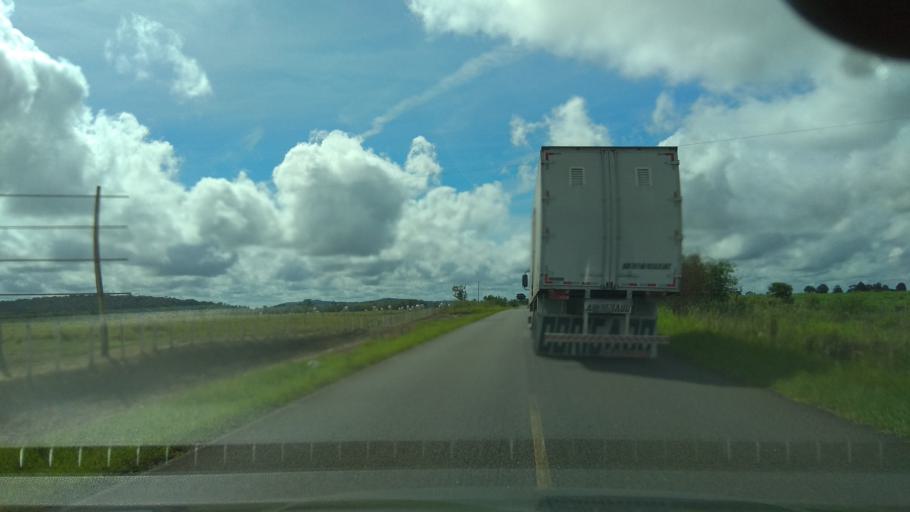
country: BR
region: Bahia
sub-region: Mutuipe
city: Mutuipe
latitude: -13.1690
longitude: -39.3460
